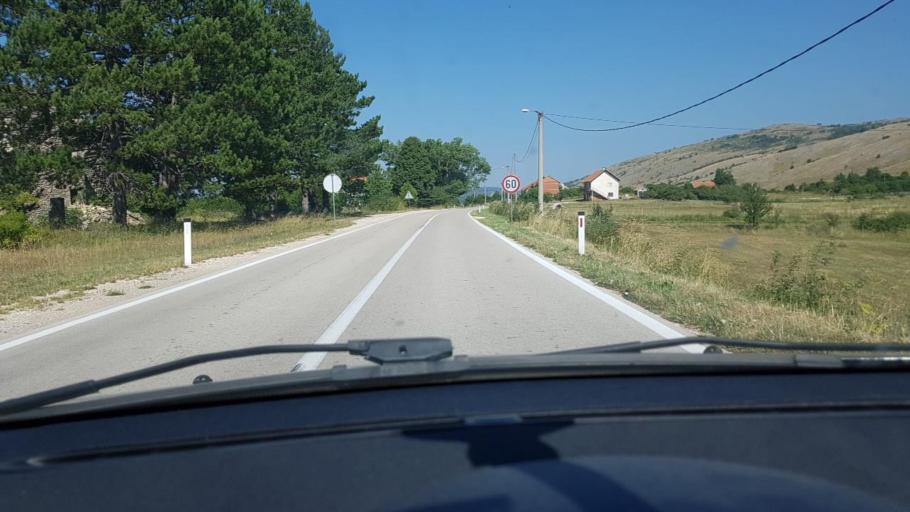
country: BA
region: Federation of Bosnia and Herzegovina
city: Bosansko Grahovo
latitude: 44.1193
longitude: 16.5358
